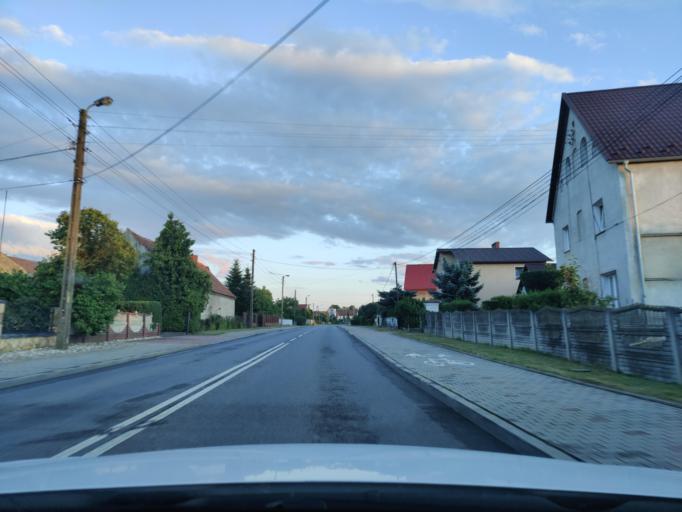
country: PL
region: Opole Voivodeship
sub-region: Powiat brzeski
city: Grodkow
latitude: 50.6608
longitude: 17.3894
